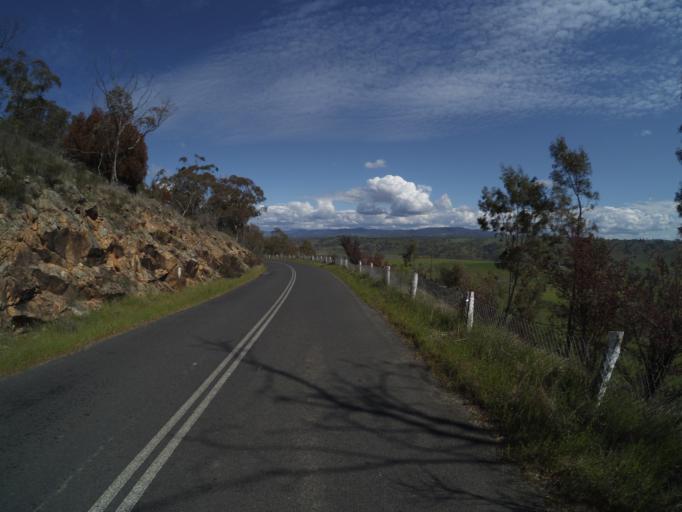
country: AU
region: New South Wales
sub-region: Yass Valley
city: Yass
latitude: -34.9873
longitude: 148.8410
